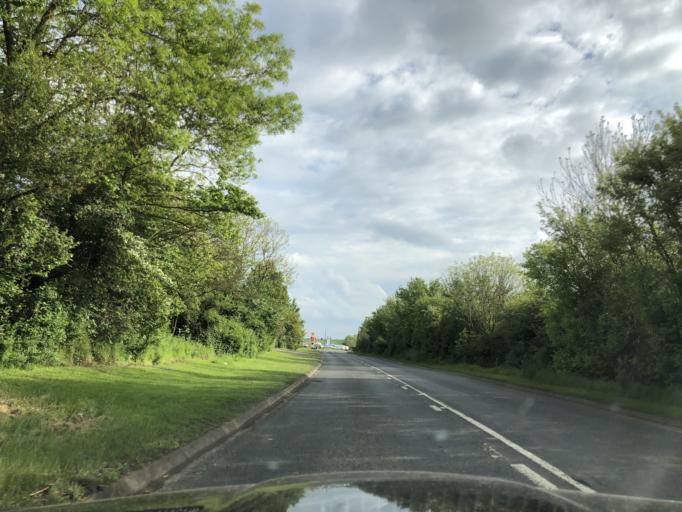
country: GB
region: England
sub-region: Warwickshire
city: Shipston on Stour
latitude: 52.0517
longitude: -1.6647
